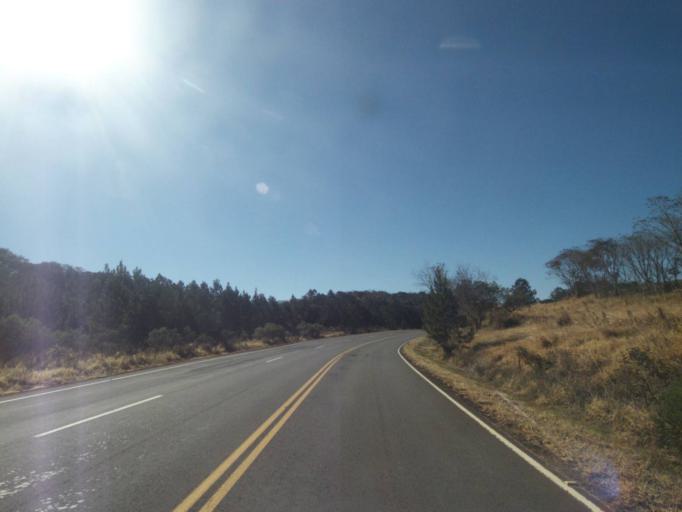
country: BR
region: Parana
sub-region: Tibagi
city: Tibagi
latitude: -24.4674
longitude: -50.4971
